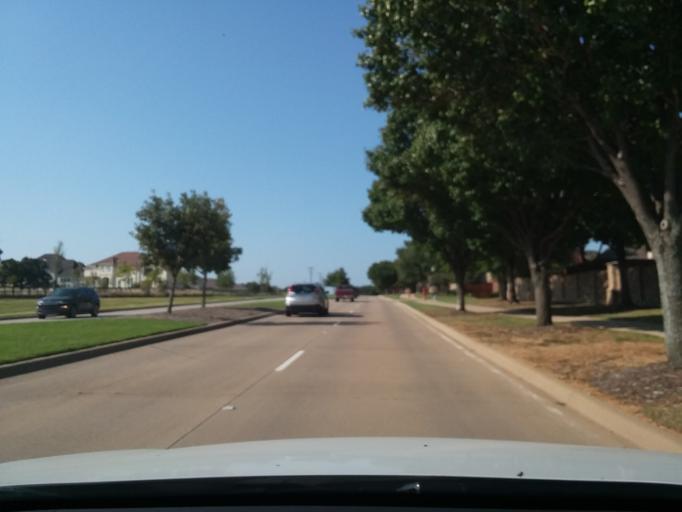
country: US
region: Texas
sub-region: Denton County
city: Flower Mound
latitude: 33.0328
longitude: -97.1051
